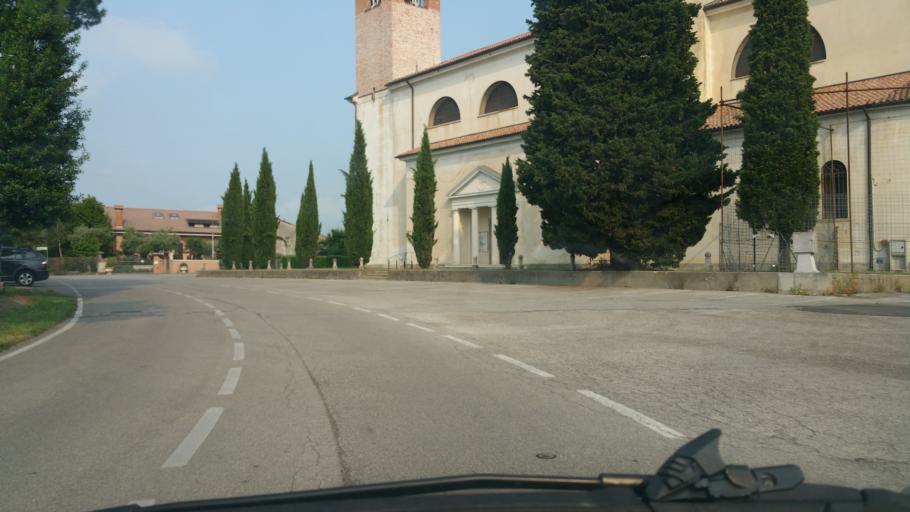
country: IT
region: Veneto
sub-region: Provincia di Treviso
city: Volpago del Montello
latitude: 45.7765
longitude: 12.1192
